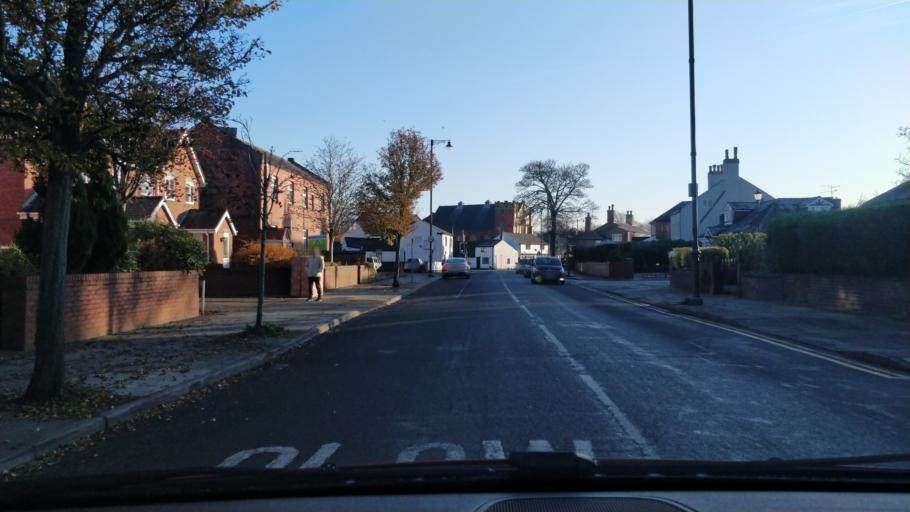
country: GB
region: England
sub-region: Sefton
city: Southport
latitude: 53.6595
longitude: -2.9653
